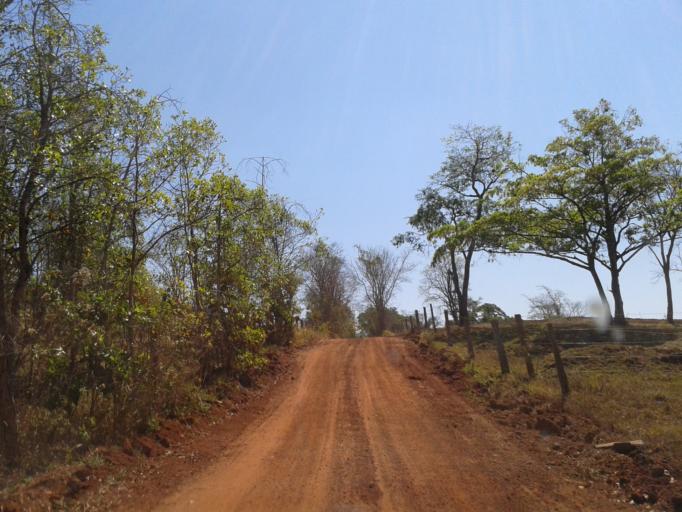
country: BR
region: Minas Gerais
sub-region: Ituiutaba
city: Ituiutaba
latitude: -19.0862
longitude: -49.3002
